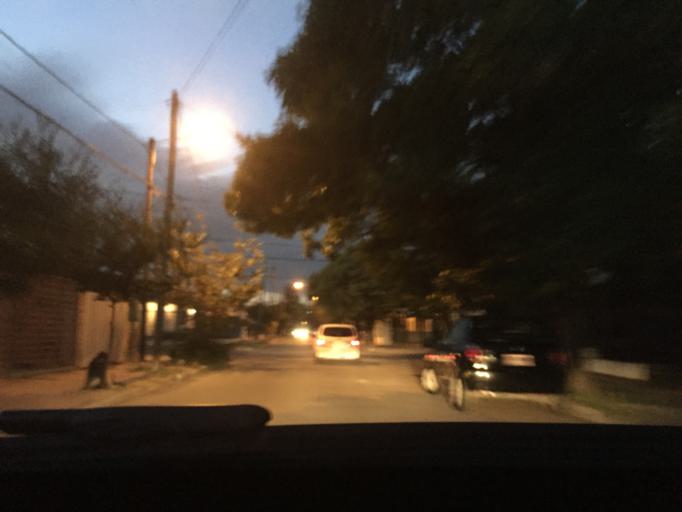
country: AR
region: Cordoba
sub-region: Departamento de Capital
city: Cordoba
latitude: -31.3640
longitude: -64.2283
